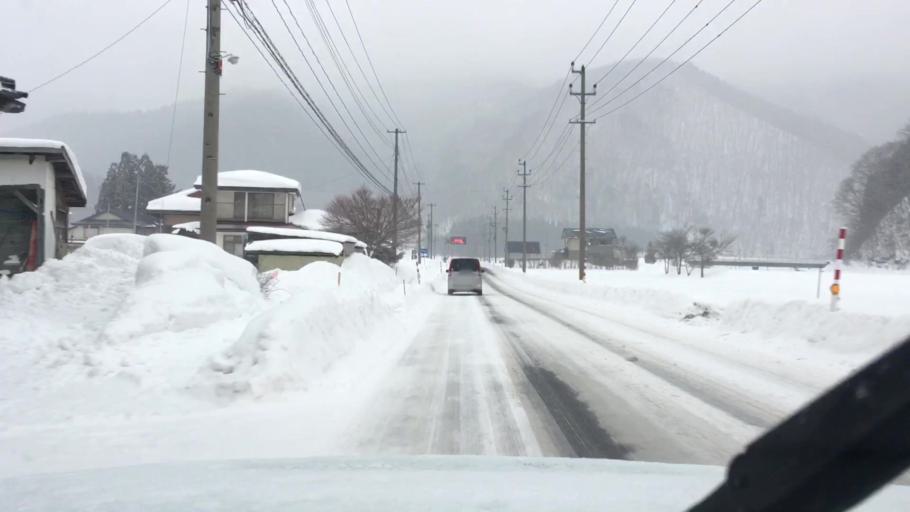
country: JP
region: Akita
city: Hanawa
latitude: 40.0770
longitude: 141.0216
